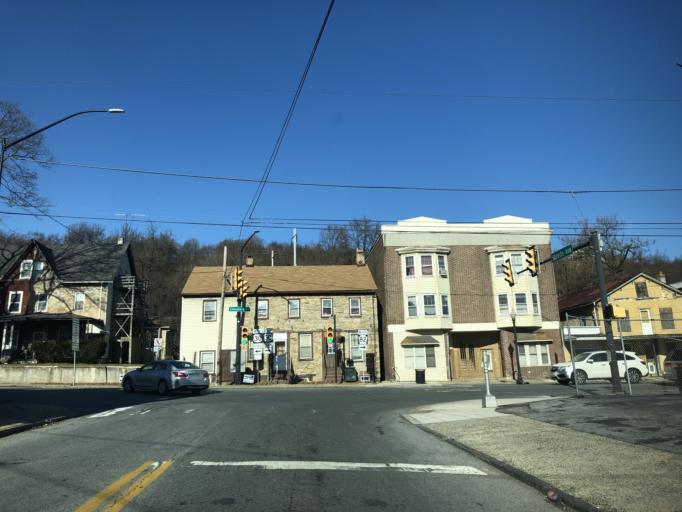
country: US
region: Pennsylvania
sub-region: Chester County
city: Coatesville
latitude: 39.9809
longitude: -75.8311
